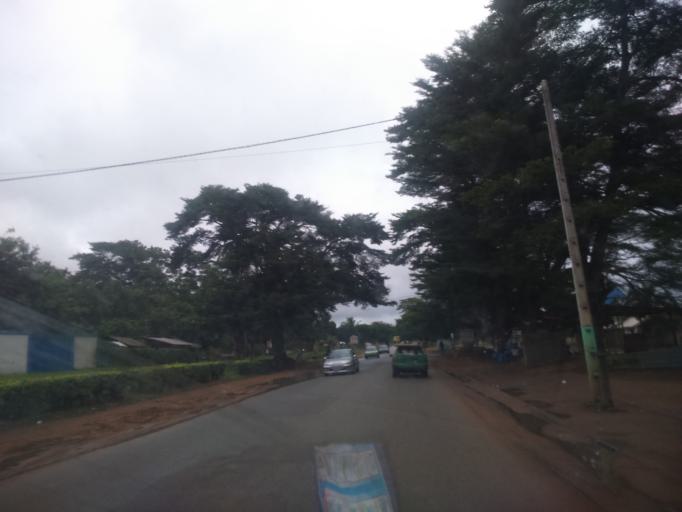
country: CI
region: Sud-Comoe
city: Bonoua
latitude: 5.2736
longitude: -3.5900
